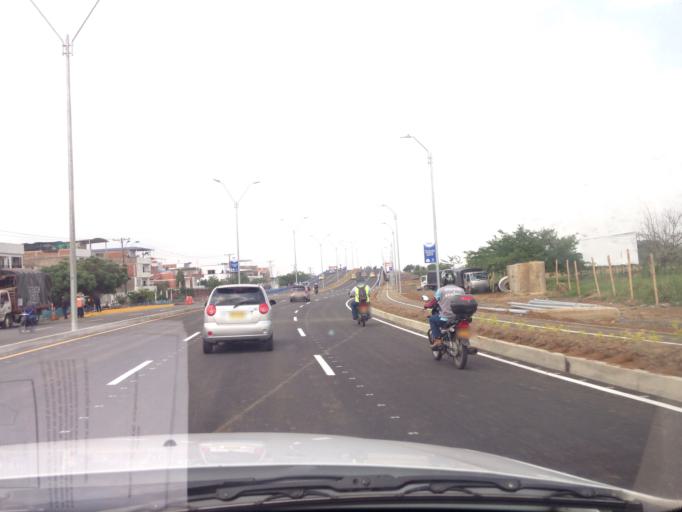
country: CO
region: Valle del Cauca
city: Cali
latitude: 3.3911
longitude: -76.5159
